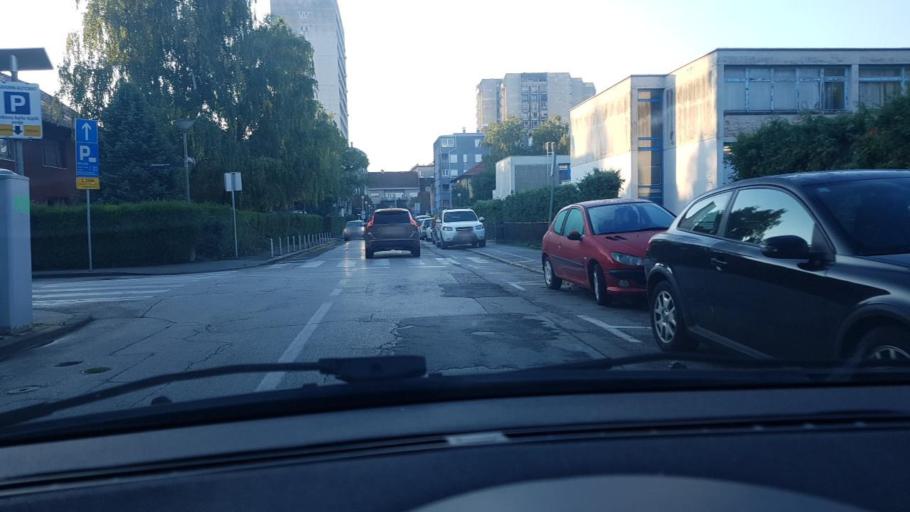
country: HR
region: Grad Zagreb
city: Zagreb
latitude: 45.8195
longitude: 16.0078
